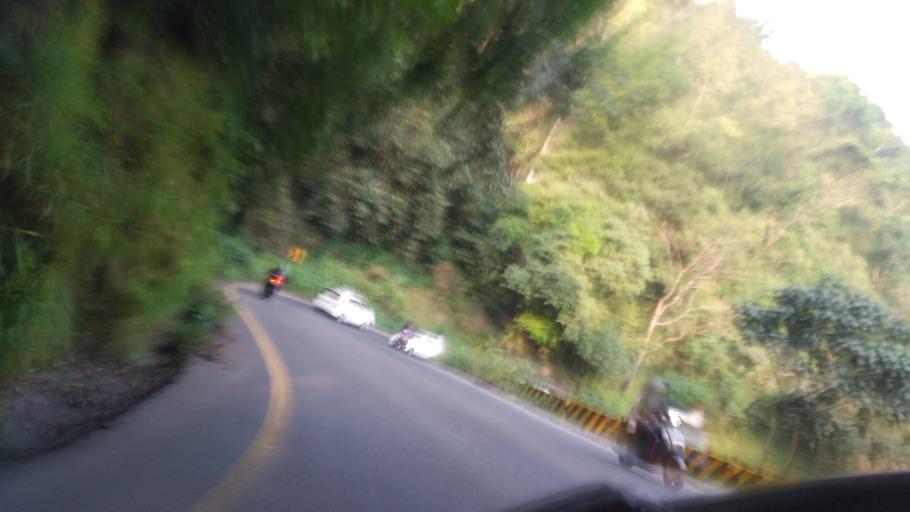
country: IN
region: Kerala
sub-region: Wayanad
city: Kalpetta
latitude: 11.5107
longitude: 76.0221
